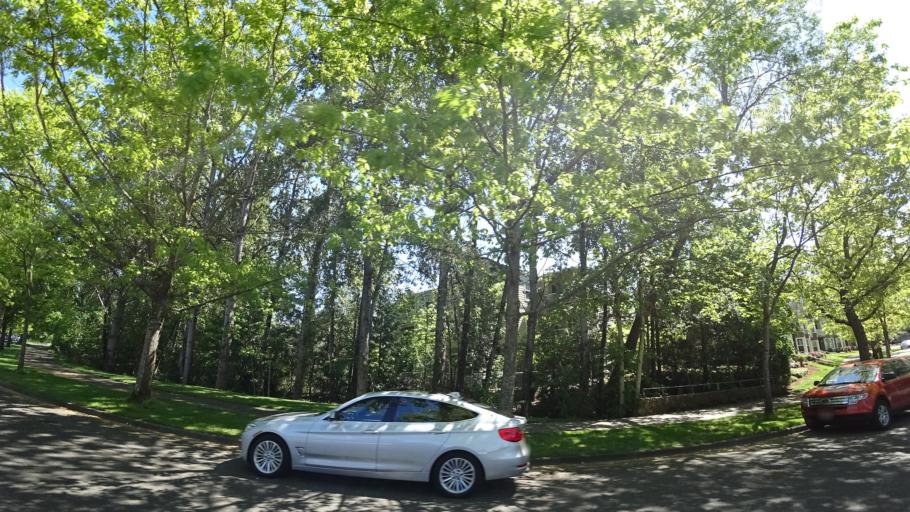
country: US
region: Oregon
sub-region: Washington County
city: Raleigh Hills
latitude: 45.4852
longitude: -122.7623
